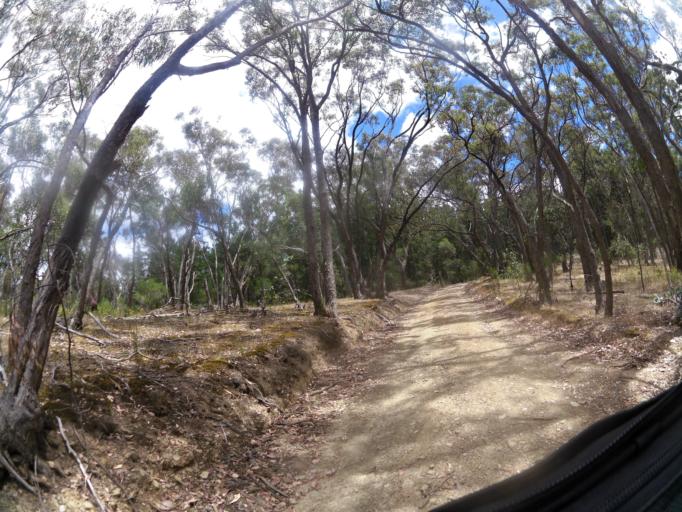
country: AU
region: Victoria
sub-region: Mount Alexander
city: Castlemaine
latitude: -37.0487
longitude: 144.2680
